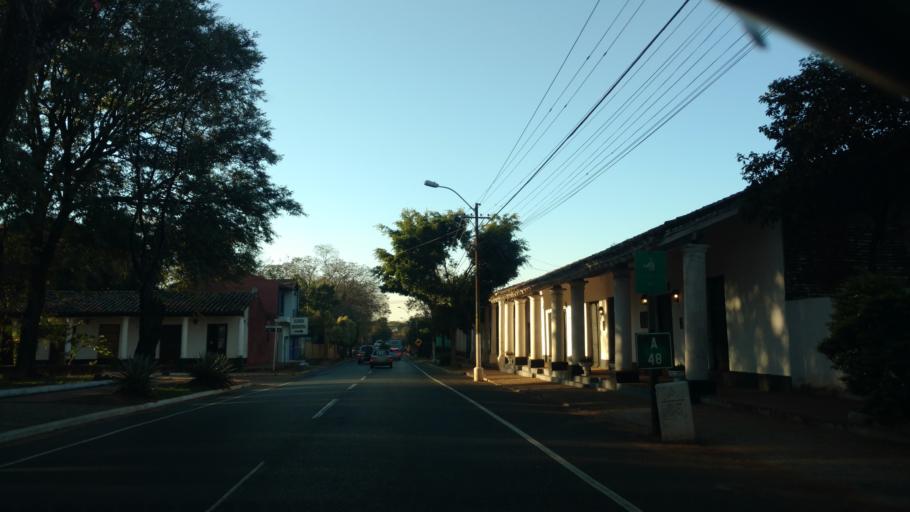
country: PY
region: Paraguari
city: Yaguaron
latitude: -25.5638
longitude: -57.2835
